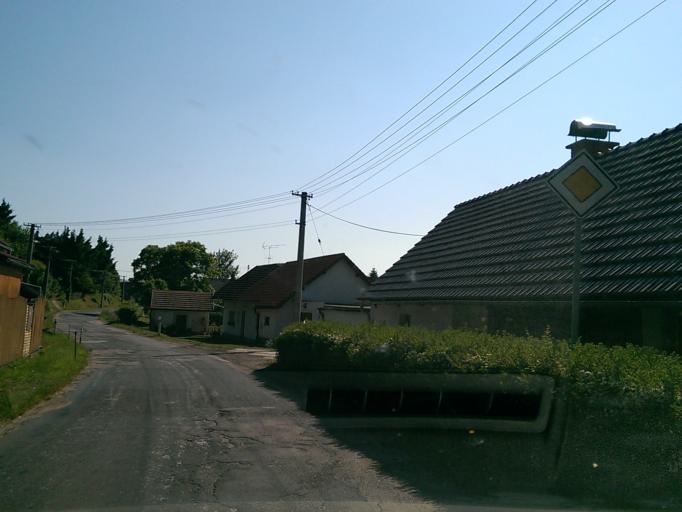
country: CZ
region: Liberecky
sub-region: Okres Semily
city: Lomnice nad Popelkou
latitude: 50.4995
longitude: 15.3221
